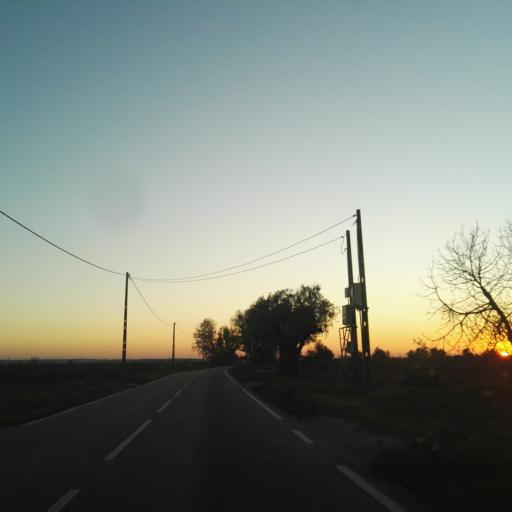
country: PT
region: Santarem
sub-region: Golega
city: Golega
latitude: 39.3222
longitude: -8.5097
